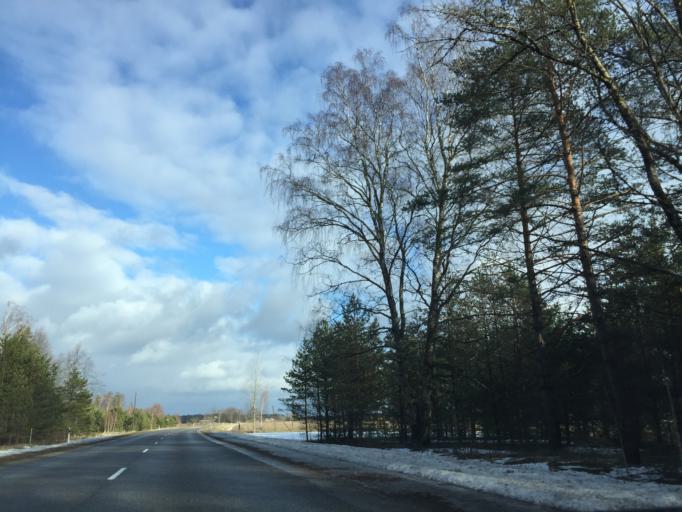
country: LV
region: Salacgrivas
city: Ainazi
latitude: 57.8617
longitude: 24.5405
